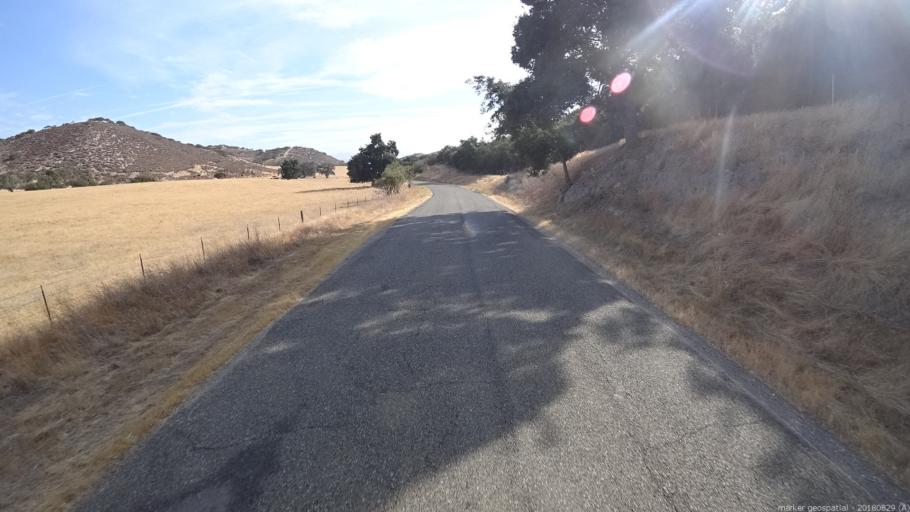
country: US
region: California
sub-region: Monterey County
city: King City
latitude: 36.0581
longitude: -121.0494
